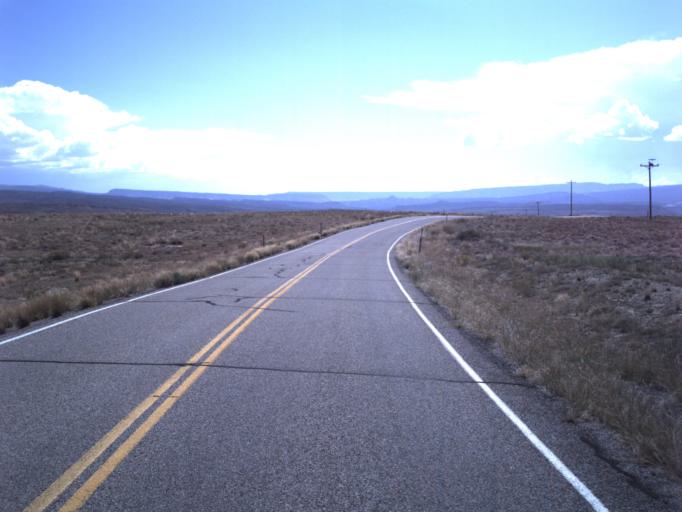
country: US
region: Utah
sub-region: Grand County
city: Moab
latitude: 38.9141
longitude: -109.3268
